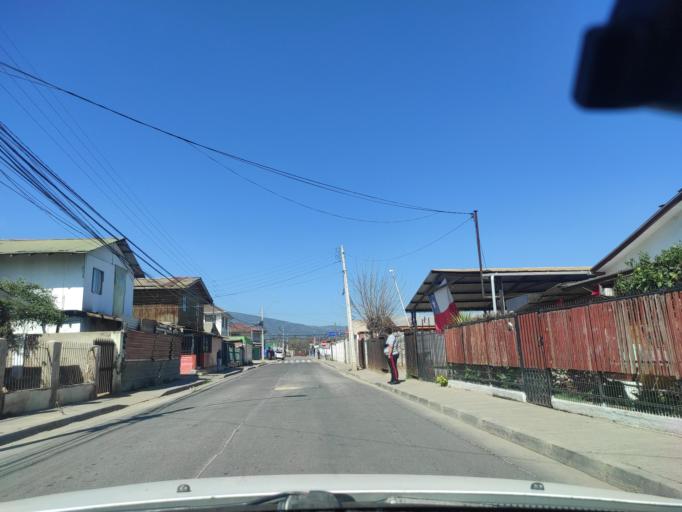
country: CL
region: Valparaiso
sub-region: Provincia de Marga Marga
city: Limache
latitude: -33.0145
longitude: -71.2639
